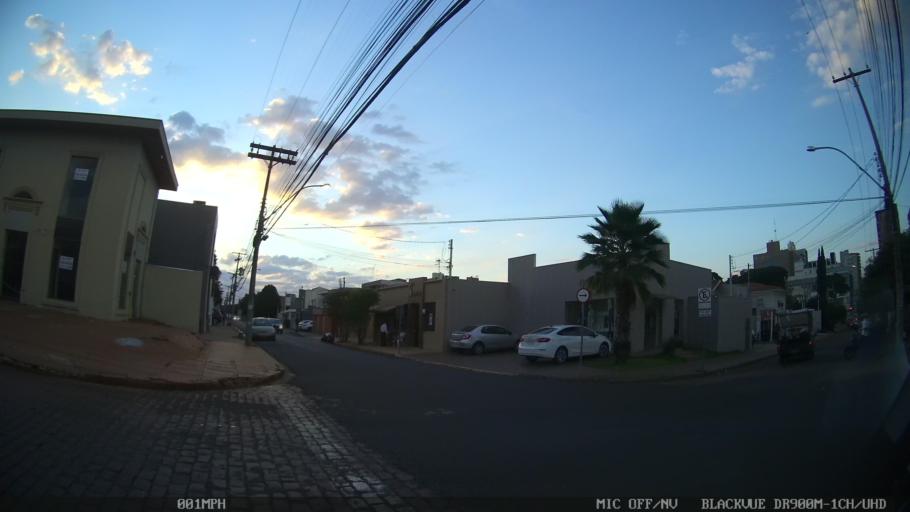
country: BR
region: Sao Paulo
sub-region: Ribeirao Preto
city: Ribeirao Preto
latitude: -21.1877
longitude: -47.8094
